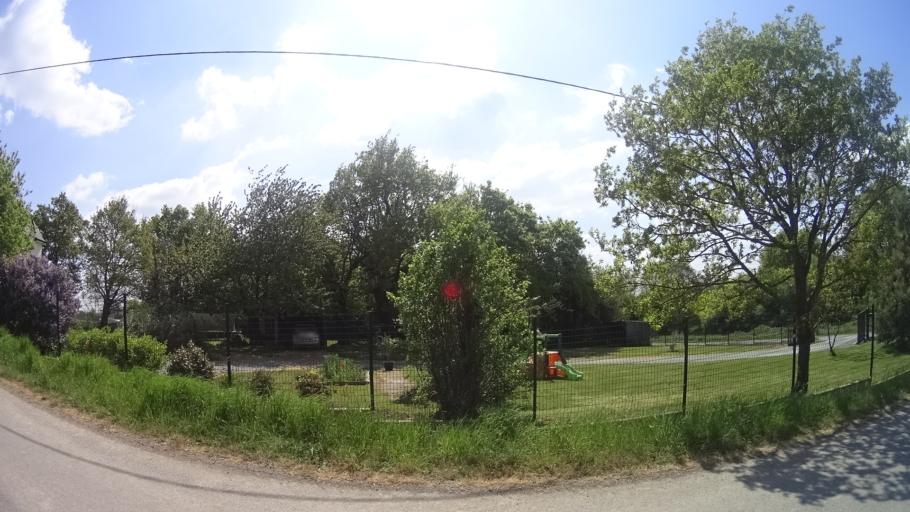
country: FR
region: Brittany
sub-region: Departement du Morbihan
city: Allaire
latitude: 47.5983
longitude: -2.1565
